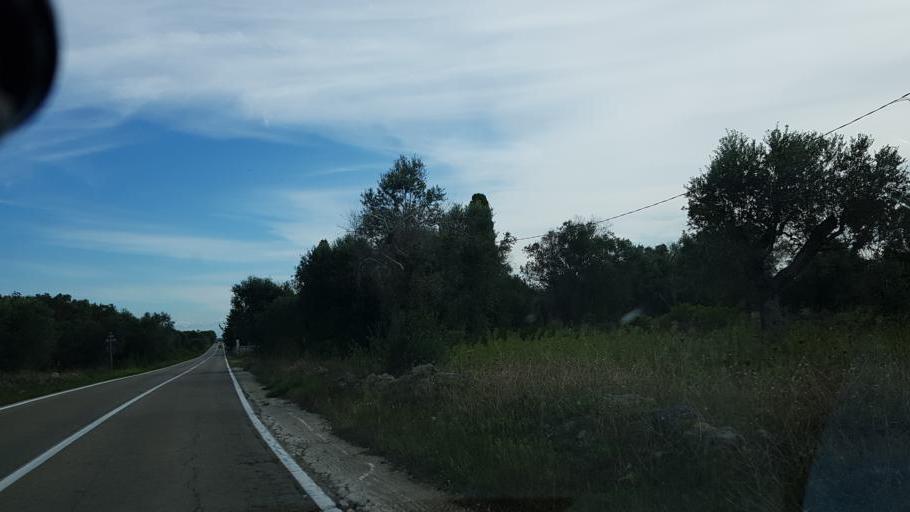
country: IT
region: Apulia
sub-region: Provincia di Lecce
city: Melendugno
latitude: 40.3353
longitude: 18.3486
